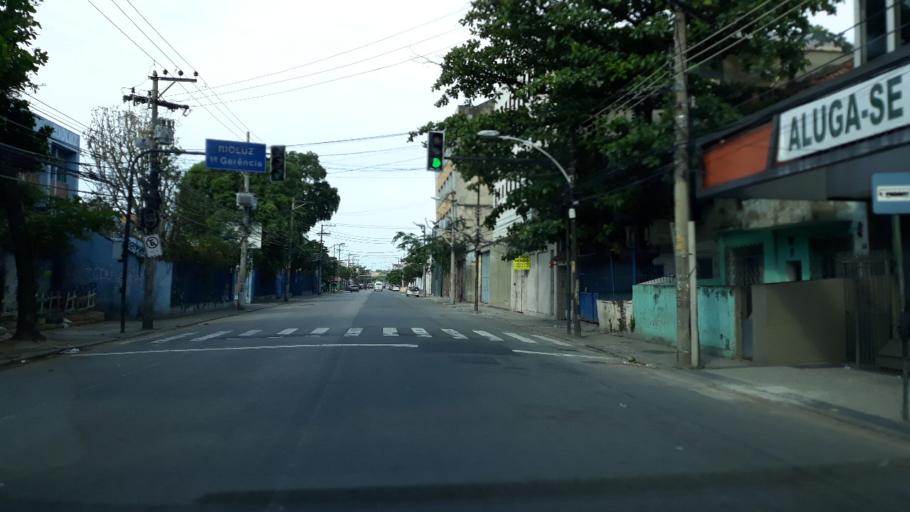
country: BR
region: Rio de Janeiro
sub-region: Rio De Janeiro
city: Rio de Janeiro
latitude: -22.8925
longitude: -43.2370
